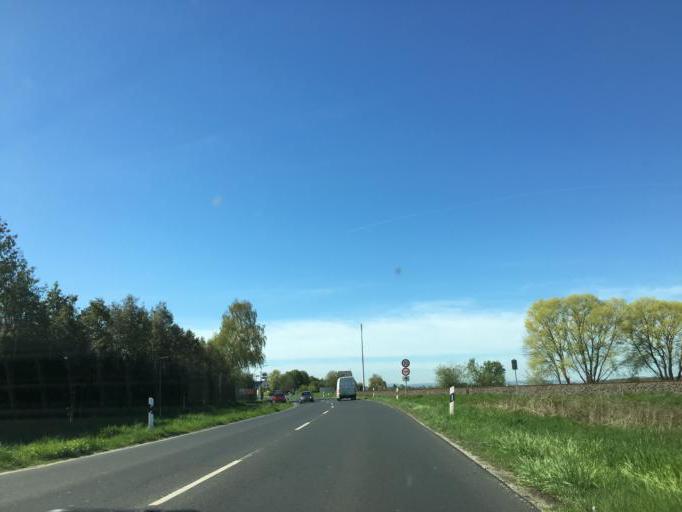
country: DE
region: Hesse
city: Gross-Umstadt
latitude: 49.8975
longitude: 8.9430
